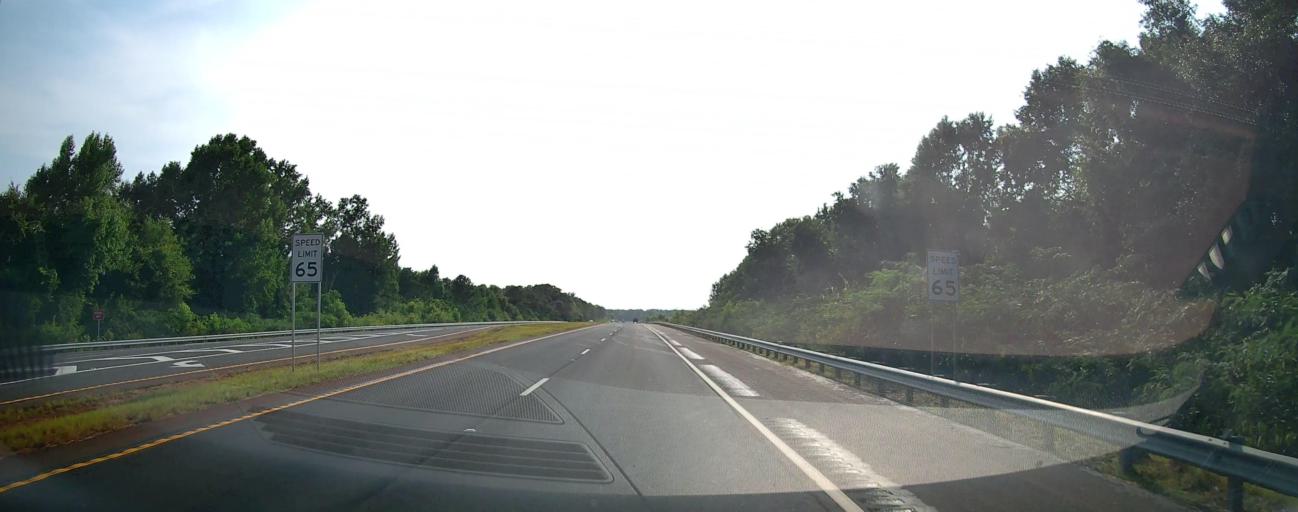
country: US
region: Georgia
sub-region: Peach County
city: Fort Valley
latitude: 32.5718
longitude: -83.9164
